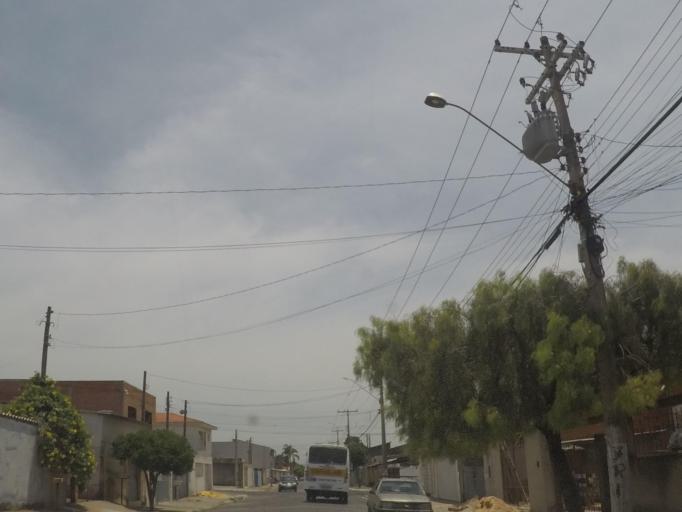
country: BR
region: Sao Paulo
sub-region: Hortolandia
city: Hortolandia
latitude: -22.8409
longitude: -47.1945
